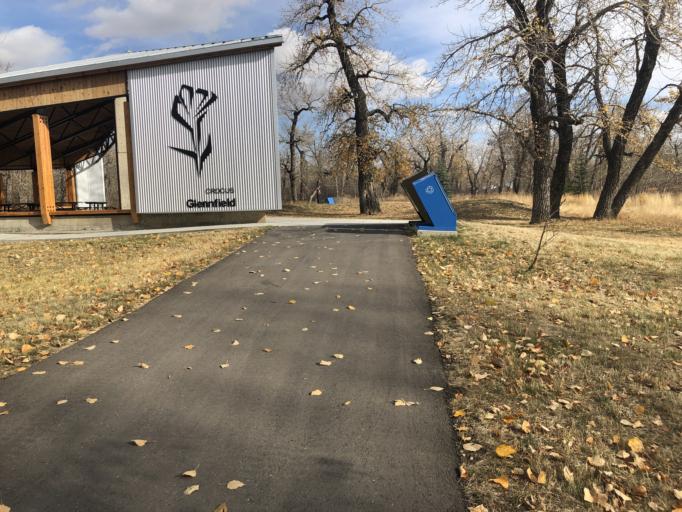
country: CA
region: Alberta
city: Calgary
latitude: 50.9280
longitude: -114.0668
